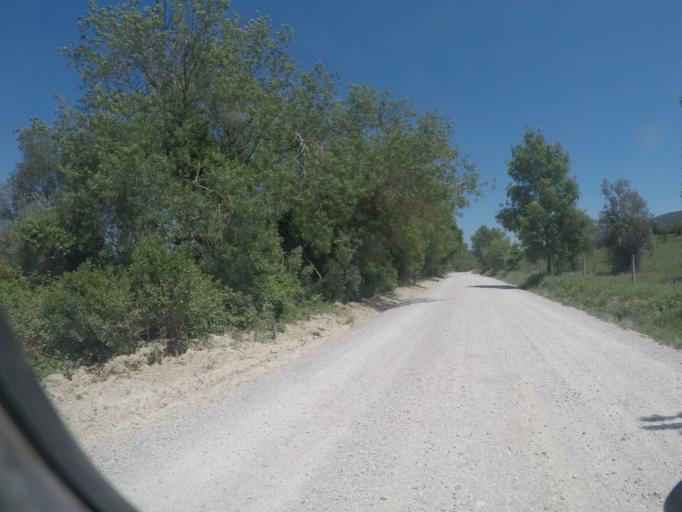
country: PT
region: Setubal
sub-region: Sesimbra
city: Sesimbra
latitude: 38.4640
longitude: -9.0511
